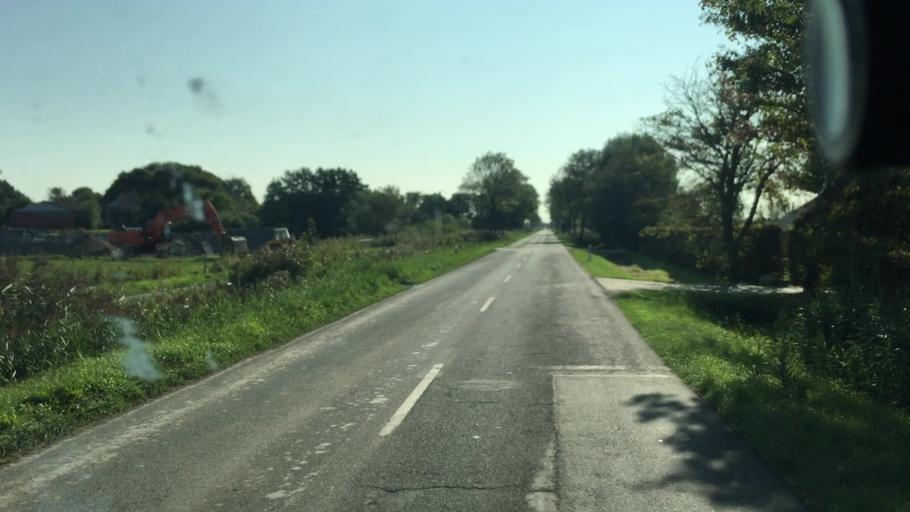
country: DE
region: Lower Saxony
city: Werdum
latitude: 53.6638
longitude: 7.6957
